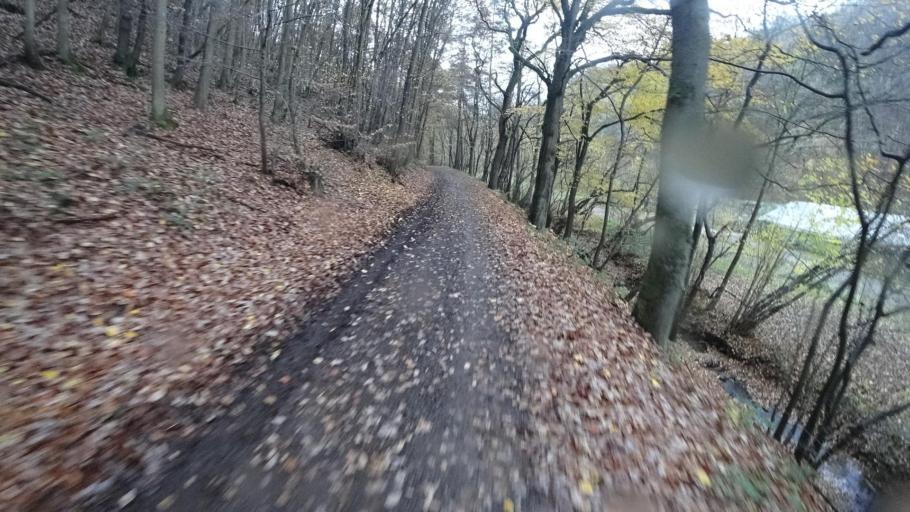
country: DE
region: Rheinland-Pfalz
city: Bad Neuenahr-Ahrweiler
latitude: 50.5218
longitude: 7.0926
